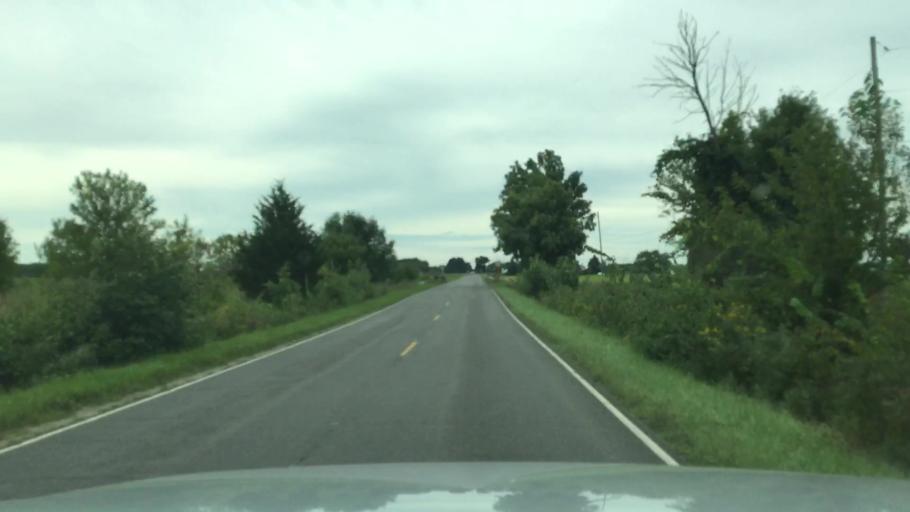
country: US
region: Michigan
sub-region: Shiawassee County
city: Durand
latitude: 43.0358
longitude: -83.9873
